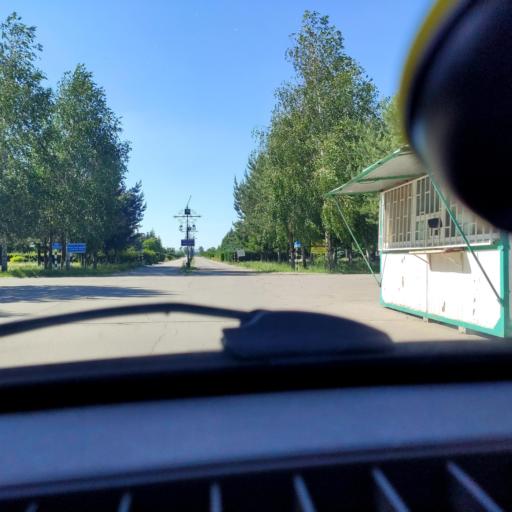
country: RU
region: Samara
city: Tol'yatti
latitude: 53.5758
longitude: 49.4252
